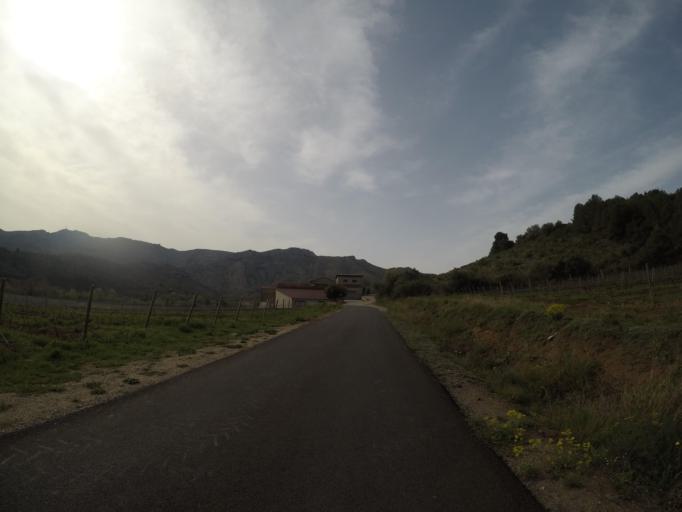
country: FR
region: Languedoc-Roussillon
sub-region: Departement des Pyrenees-Orientales
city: Baixas
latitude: 42.7790
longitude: 2.7643
